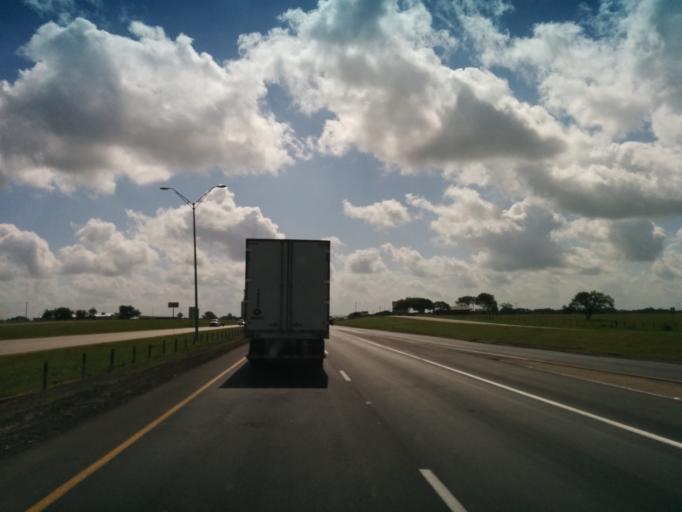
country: US
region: Texas
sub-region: Colorado County
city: Weimar
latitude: 29.6918
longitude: -96.7740
